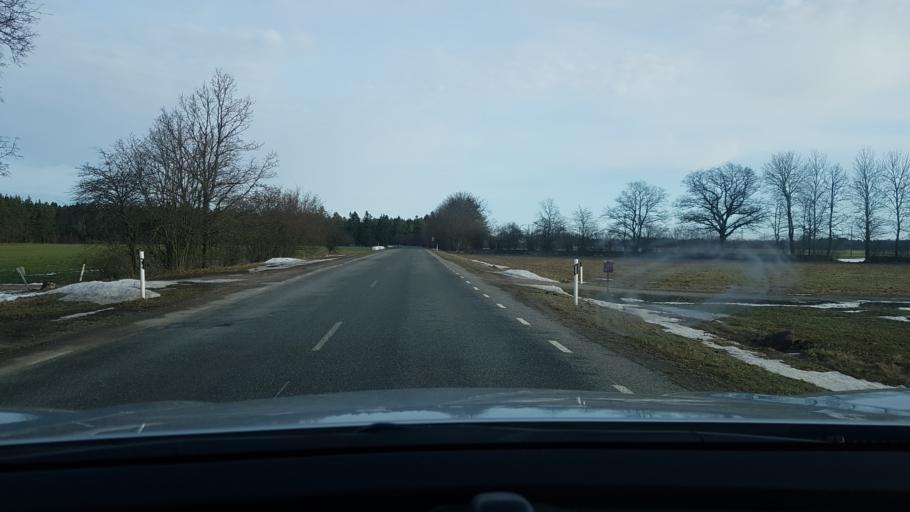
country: EE
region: Saare
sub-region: Kuressaare linn
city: Kuressaare
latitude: 58.4071
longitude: 22.6503
